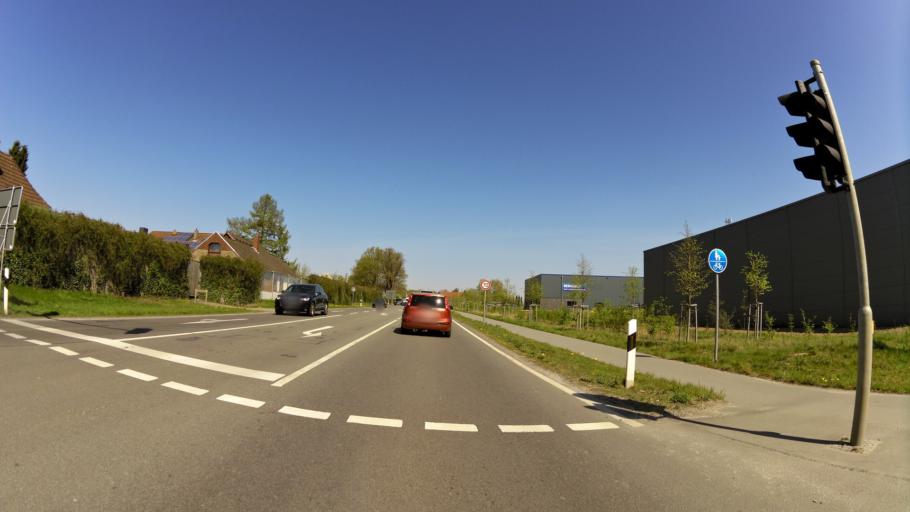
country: DE
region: Lower Saxony
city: Ganderkesee
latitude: 53.0609
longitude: 8.5299
